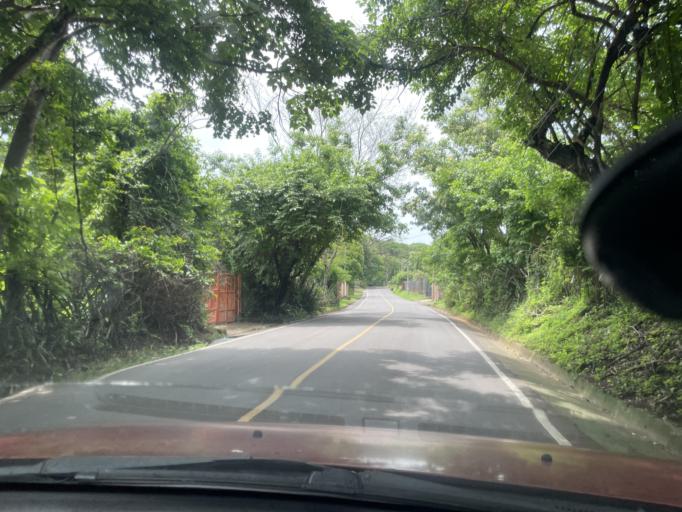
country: SV
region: La Union
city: Santa Rosa de Lima
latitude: 13.6511
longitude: -87.8430
